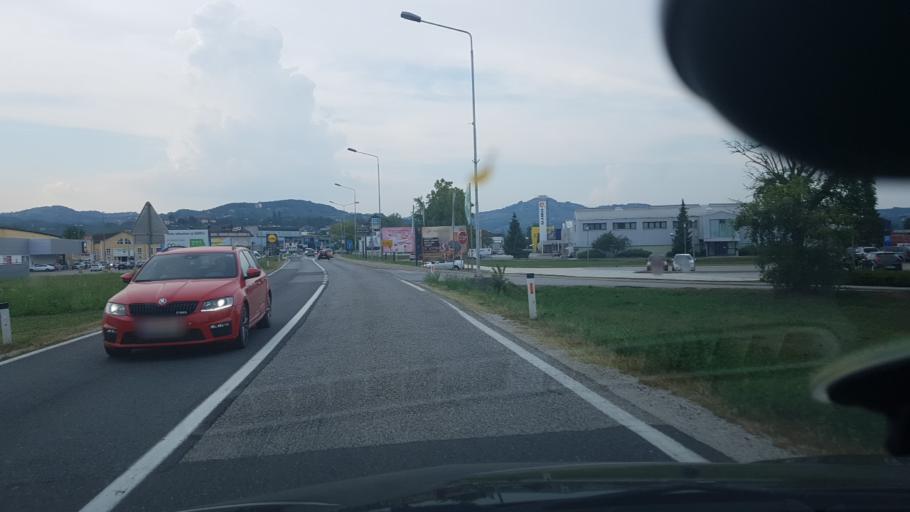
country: SI
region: Krsko
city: Leskovec pri Krskem
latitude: 45.9361
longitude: 15.4851
